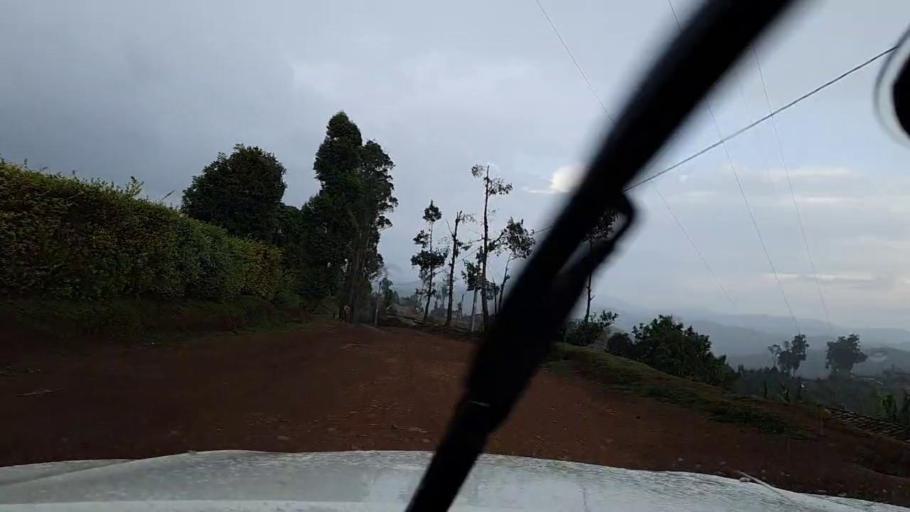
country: BI
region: Kayanza
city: Kayanza
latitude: -2.7800
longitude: 29.5353
